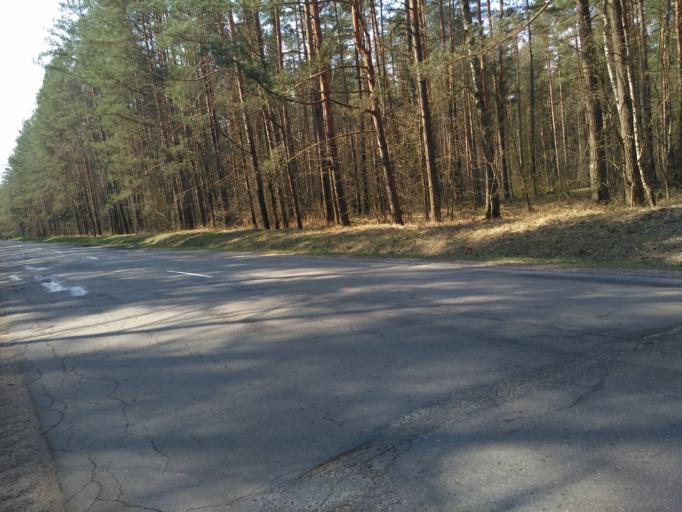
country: BY
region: Minsk
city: Zamostochcha
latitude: 53.8998
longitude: 27.9292
